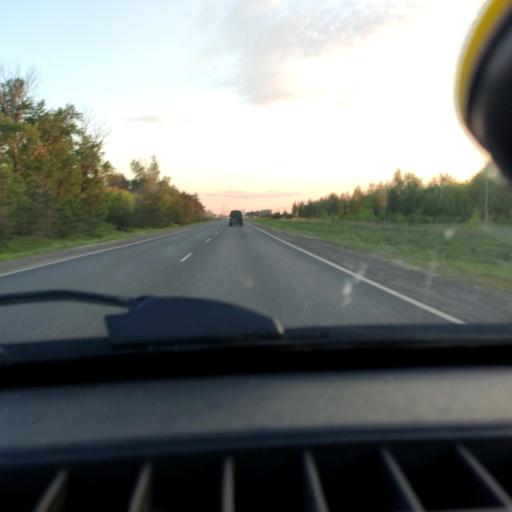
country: RU
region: Samara
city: Povolzhskiy
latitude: 53.5959
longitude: 49.5870
